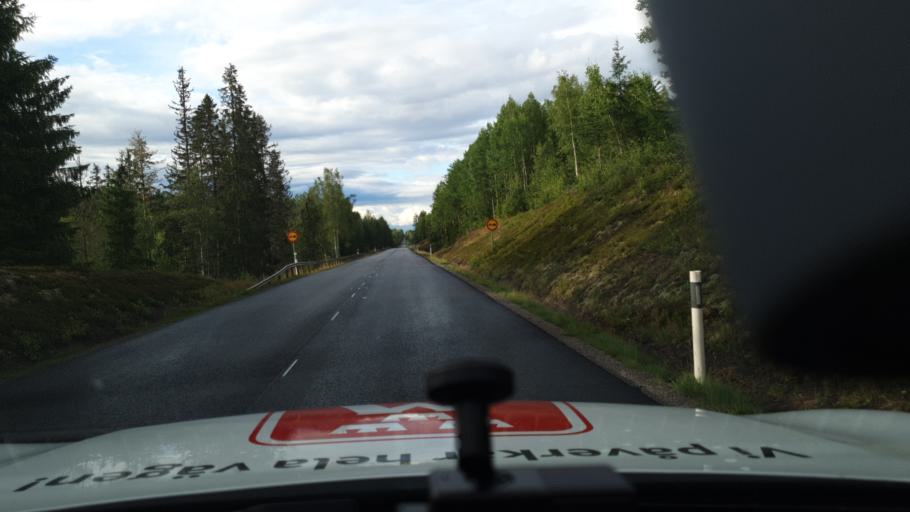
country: SE
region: Vaermland
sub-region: Torsby Kommun
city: Torsby
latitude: 60.2581
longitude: 13.0236
